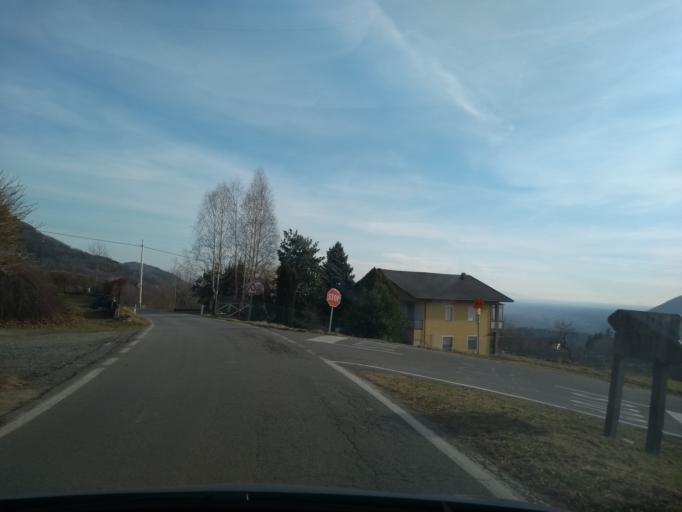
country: IT
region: Piedmont
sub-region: Provincia di Torino
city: Lanzo Torinese
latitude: 45.2974
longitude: 7.4827
